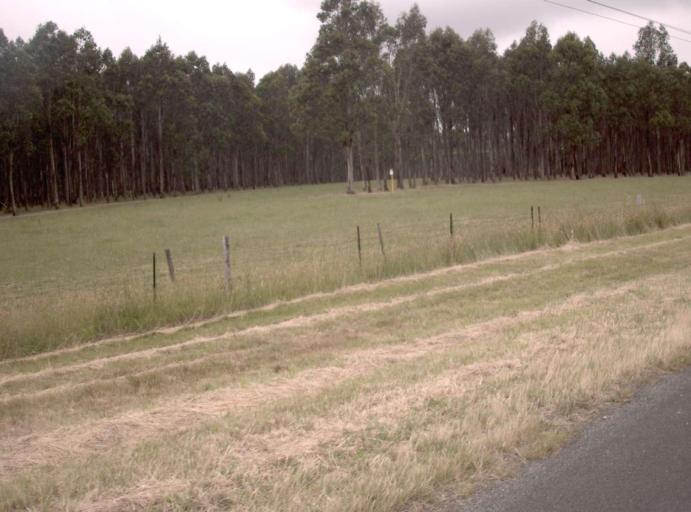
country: AU
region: Victoria
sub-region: Latrobe
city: Morwell
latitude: -38.2765
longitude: 146.4200
